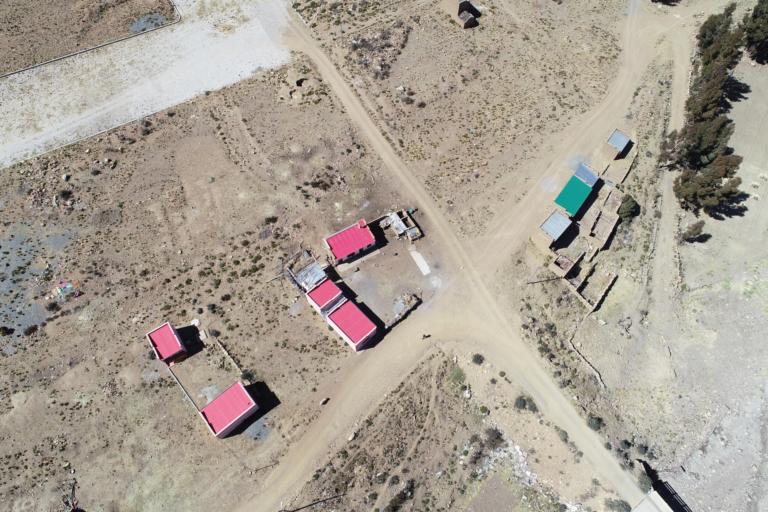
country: BO
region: La Paz
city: Achacachi
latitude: -15.8869
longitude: -68.8134
